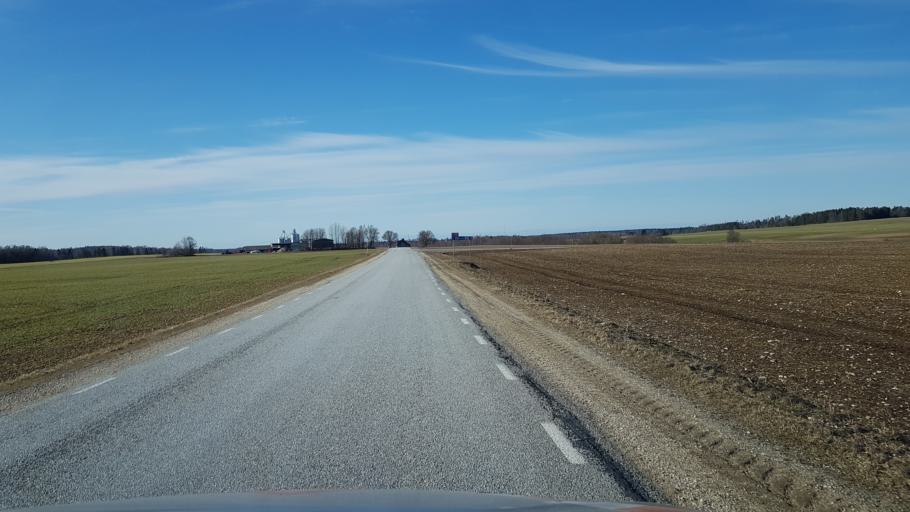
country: EE
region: Laeaene-Virumaa
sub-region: Kadrina vald
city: Kadrina
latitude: 59.2881
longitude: 26.1772
